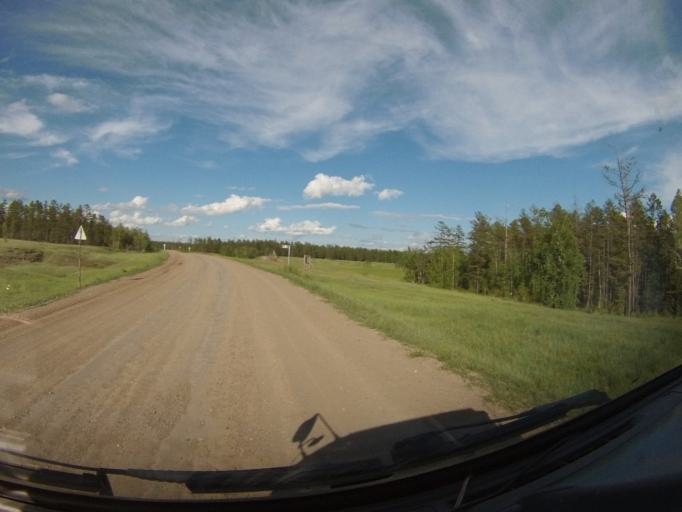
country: RU
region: Sakha
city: Ytyk-Kyuyel'
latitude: 62.2223
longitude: 133.2795
